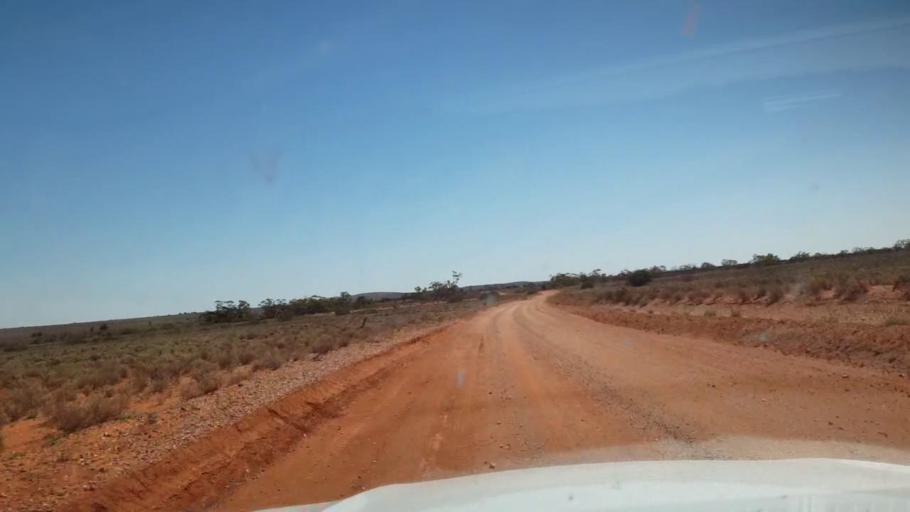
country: AU
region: South Australia
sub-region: Whyalla
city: Whyalla
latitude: -32.6857
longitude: 137.1107
